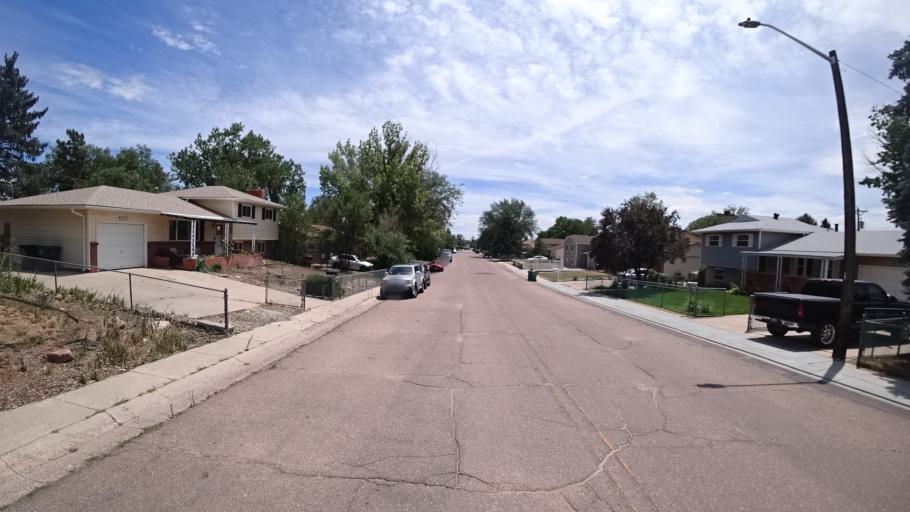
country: US
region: Colorado
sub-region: El Paso County
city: Security-Widefield
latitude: 38.7321
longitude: -104.7306
